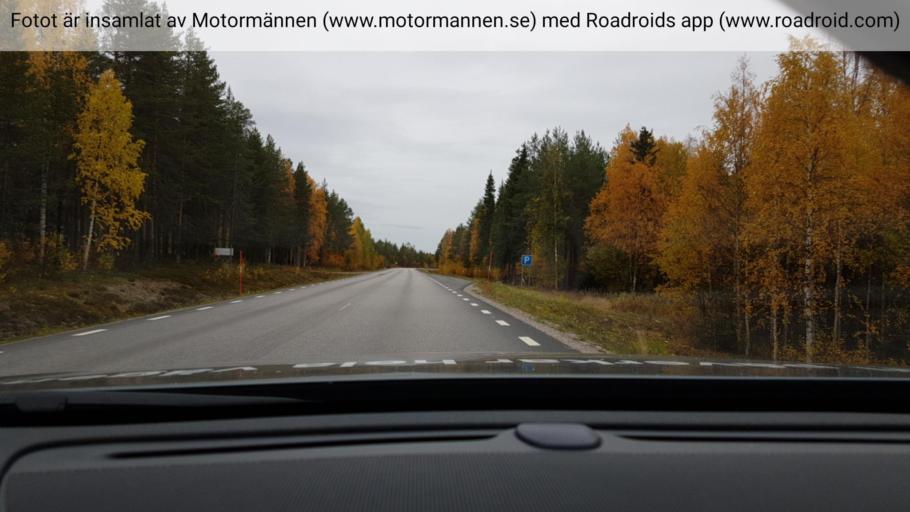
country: SE
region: Norrbotten
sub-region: Overkalix Kommun
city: OEverkalix
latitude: 66.3470
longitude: 22.8285
